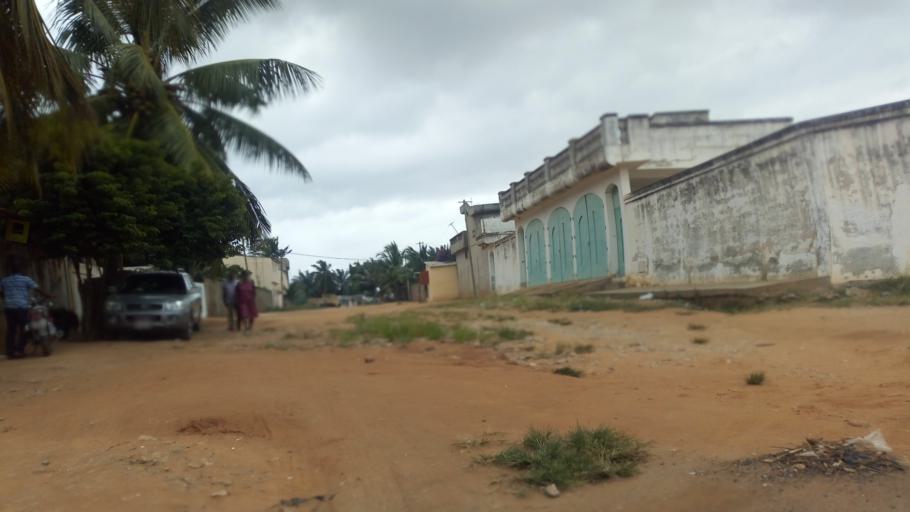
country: TG
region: Maritime
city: Lome
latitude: 6.1712
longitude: 1.1786
